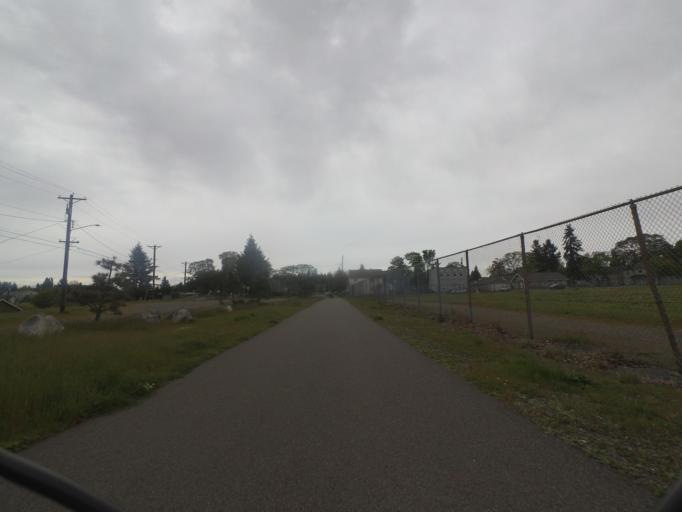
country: US
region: Washington
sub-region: Pierce County
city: Lakewood
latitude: 47.2039
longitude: -122.4769
